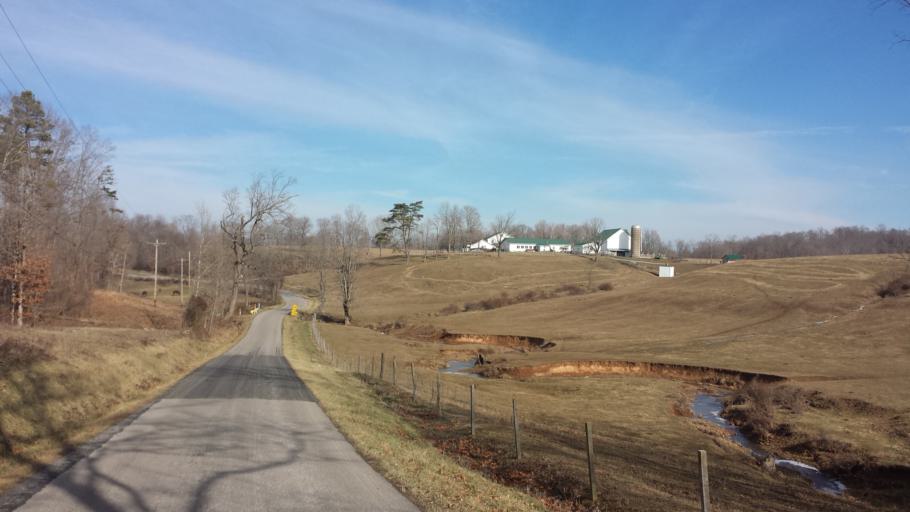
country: US
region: Ohio
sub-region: Gallia County
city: Gallipolis
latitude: 38.8271
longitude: -82.3220
